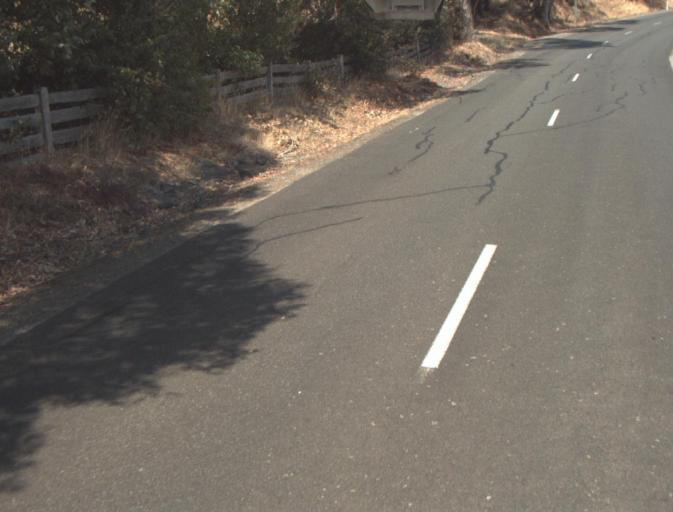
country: AU
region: Tasmania
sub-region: Launceston
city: Newstead
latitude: -41.4772
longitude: 147.1893
